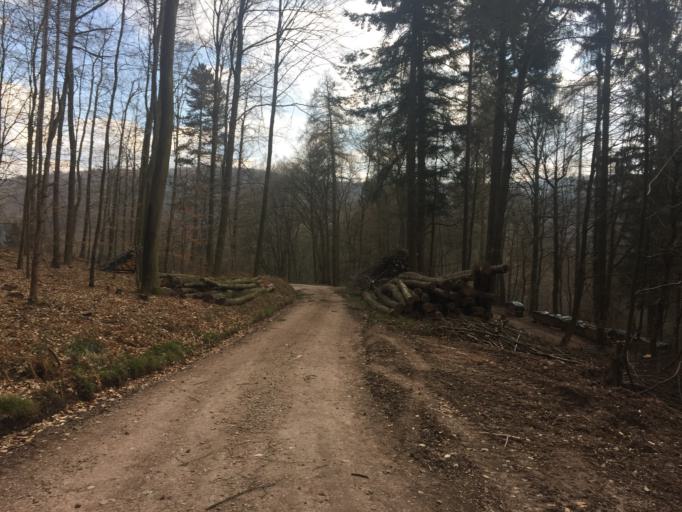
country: DE
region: Baden-Wuerttemberg
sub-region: Karlsruhe Region
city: Wilhelmsfeld
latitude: 49.4788
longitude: 8.7210
